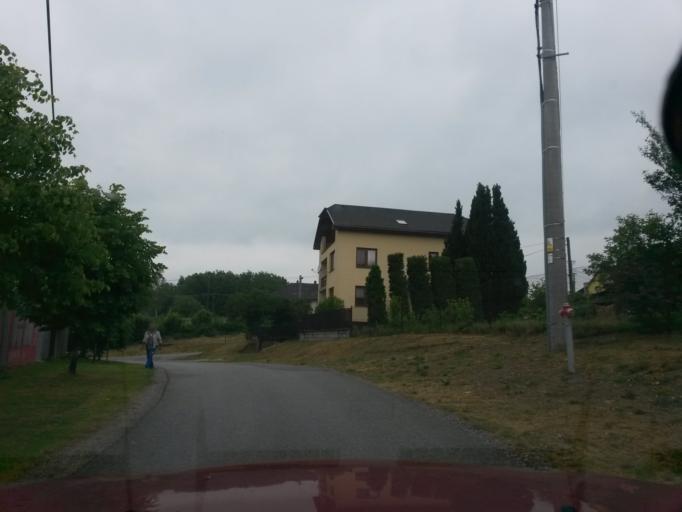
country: SK
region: Kosicky
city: Moldava nad Bodvou
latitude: 48.6939
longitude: 21.0720
